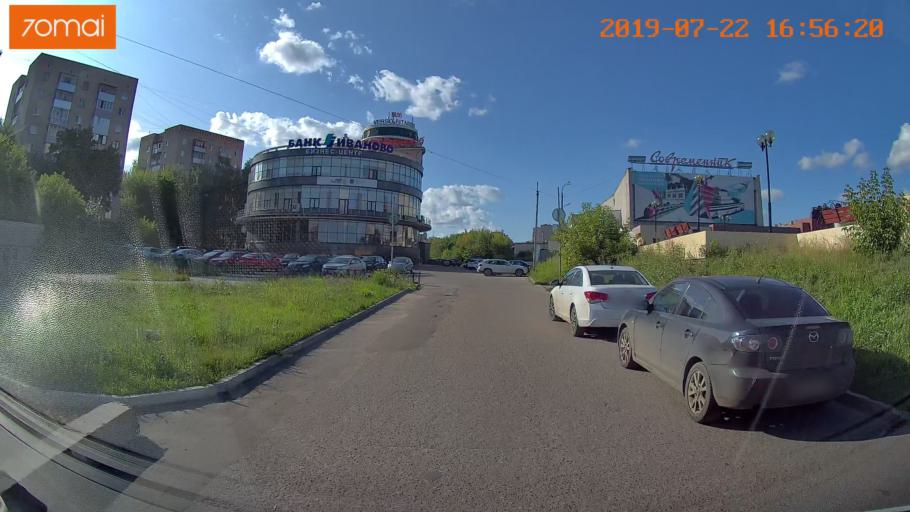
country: RU
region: Ivanovo
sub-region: Gorod Ivanovo
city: Ivanovo
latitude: 57.0067
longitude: 40.9896
